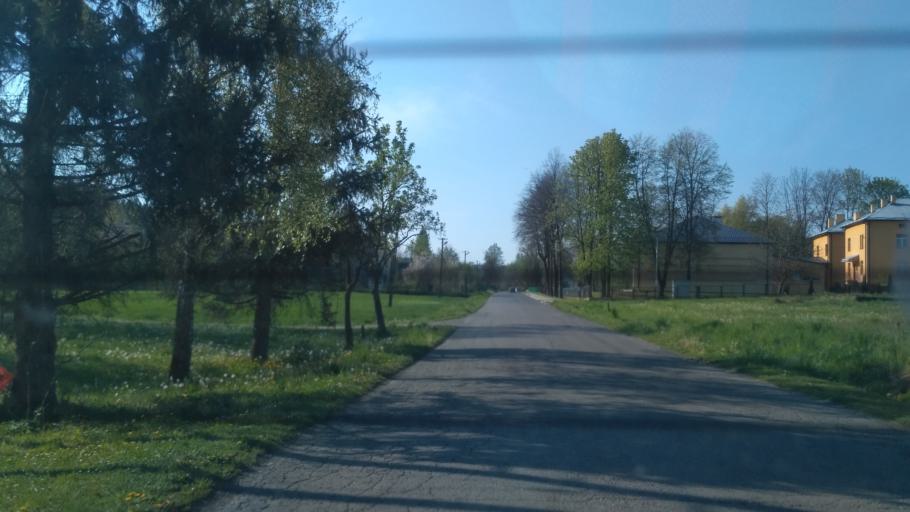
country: PL
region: Subcarpathian Voivodeship
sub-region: Powiat jaroslawski
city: Pruchnik
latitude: 49.8874
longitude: 22.5598
